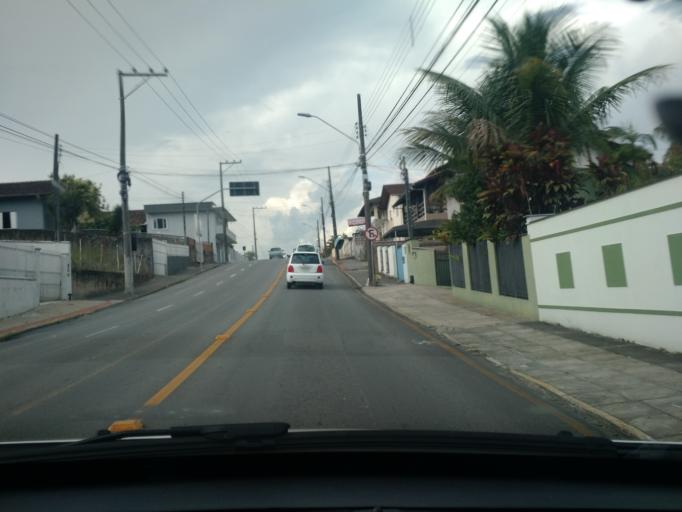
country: BR
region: Santa Catarina
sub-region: Jaragua Do Sul
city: Jaragua do Sul
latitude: -26.4944
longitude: -49.0901
